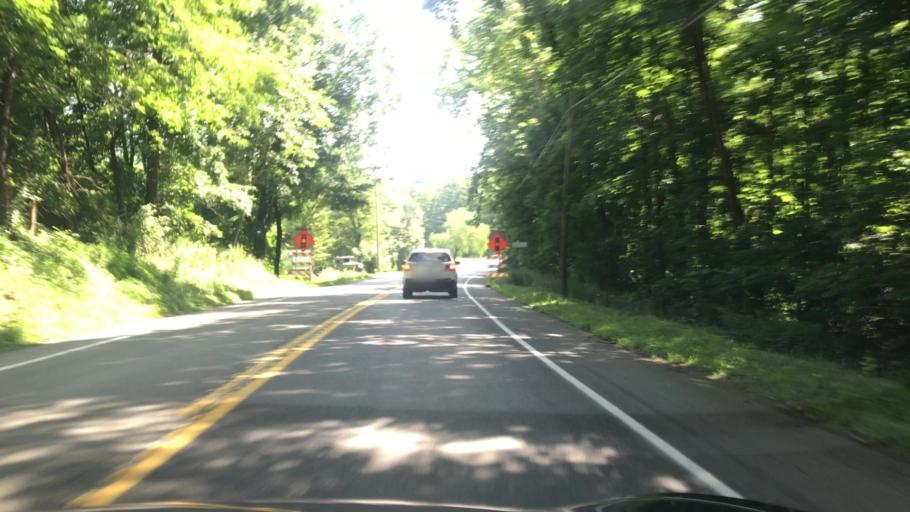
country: US
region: Pennsylvania
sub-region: Lycoming County
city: Garden View
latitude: 41.4218
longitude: -77.0287
